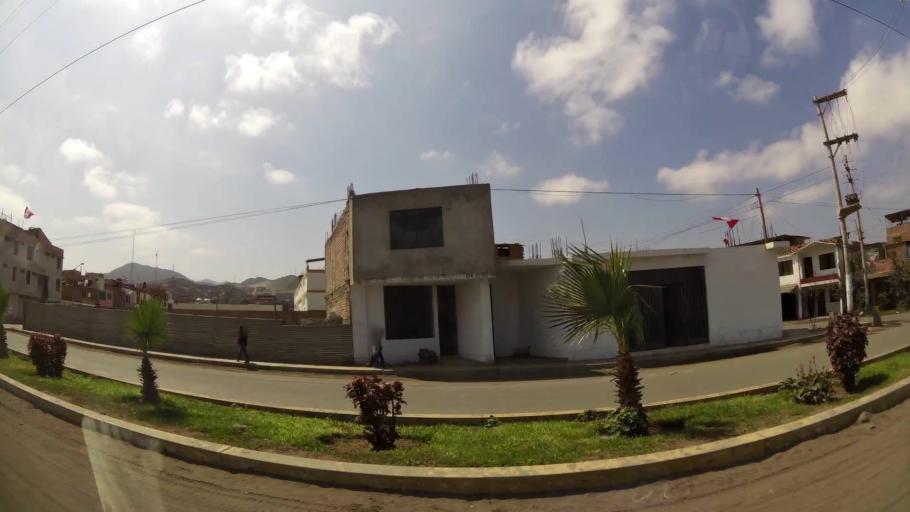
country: PE
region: Lima
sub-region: Provincia de Canete
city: Mala
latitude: -12.6639
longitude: -76.6321
